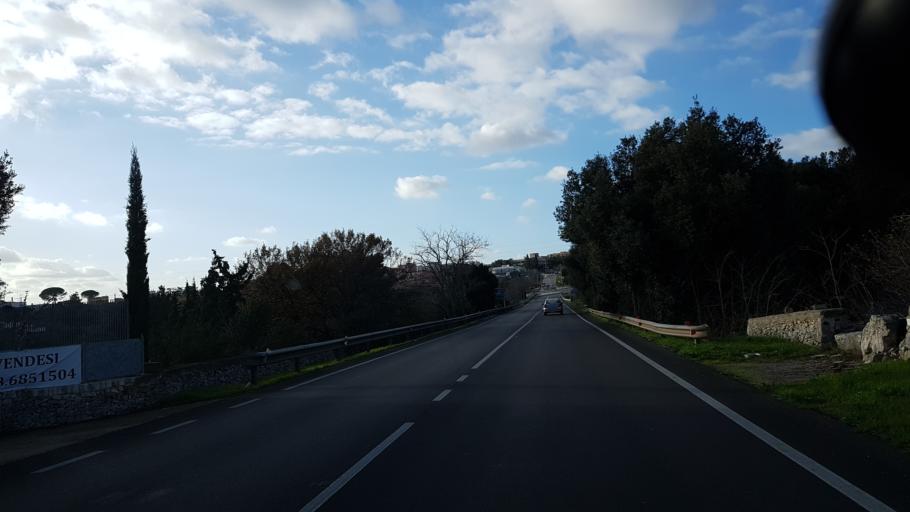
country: IT
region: Apulia
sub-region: Provincia di Bari
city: Putignano
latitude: 40.8454
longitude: 17.1351
